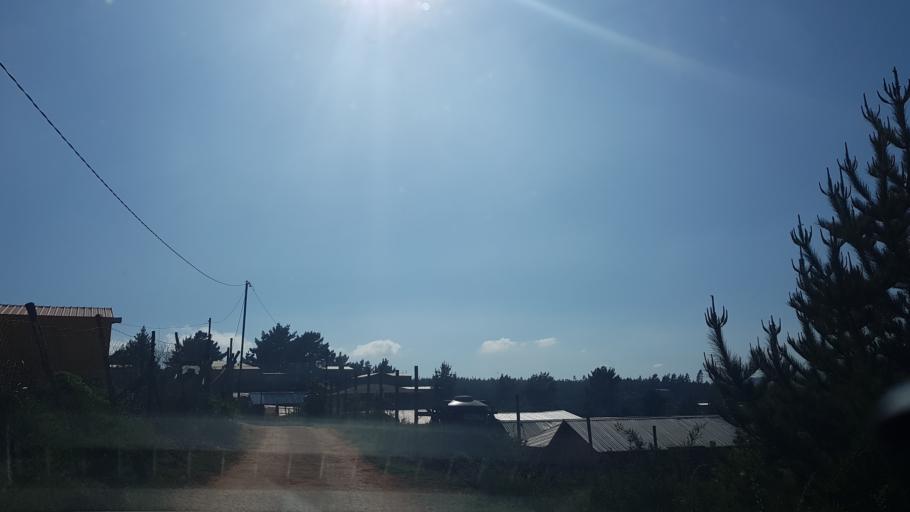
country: CL
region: Valparaiso
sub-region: Provincia de Valparaiso
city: Valparaiso
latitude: -33.1383
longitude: -71.6592
